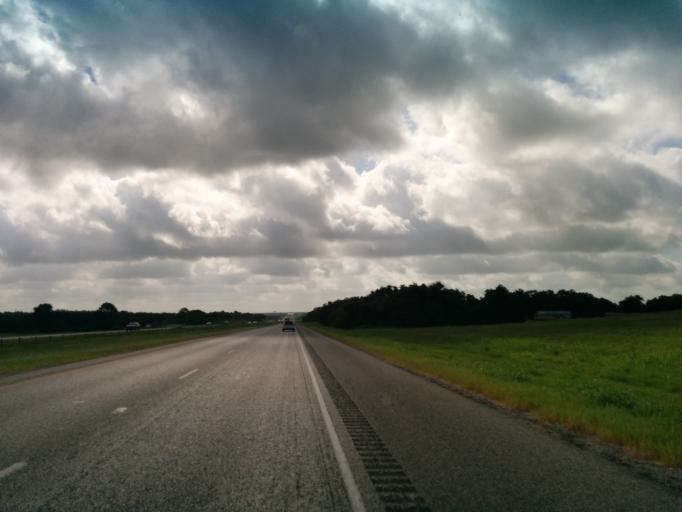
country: US
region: Texas
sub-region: Caldwell County
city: Luling
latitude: 29.6533
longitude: -97.5554
